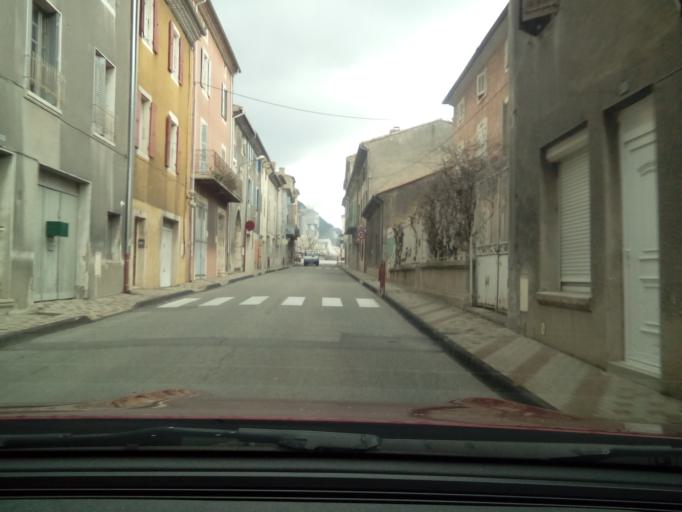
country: FR
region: Rhone-Alpes
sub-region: Departement de l'Ardeche
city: Cruas
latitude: 44.6557
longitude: 4.7622
